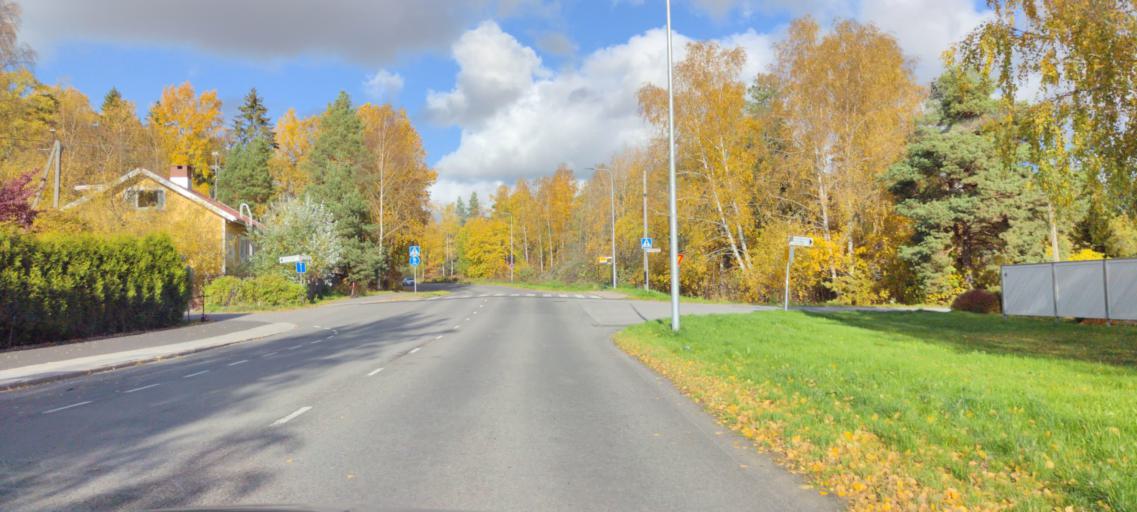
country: FI
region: Varsinais-Suomi
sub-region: Turku
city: Turku
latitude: 60.4225
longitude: 22.2704
